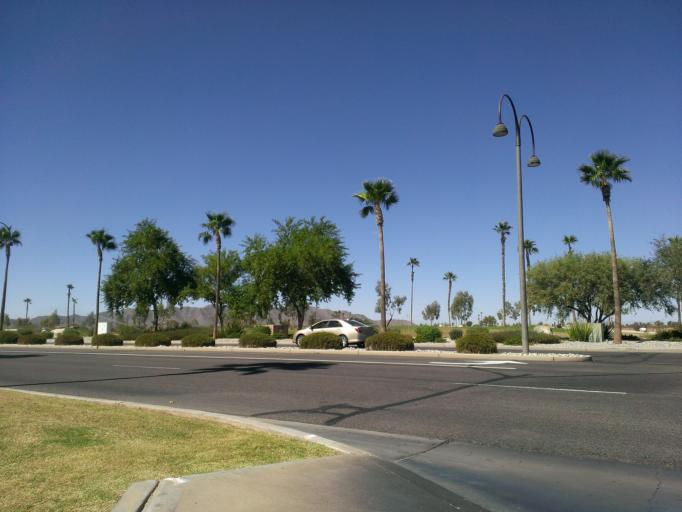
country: US
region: Arizona
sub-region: Pinal County
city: Arizona City
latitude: 32.8122
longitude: -111.6460
